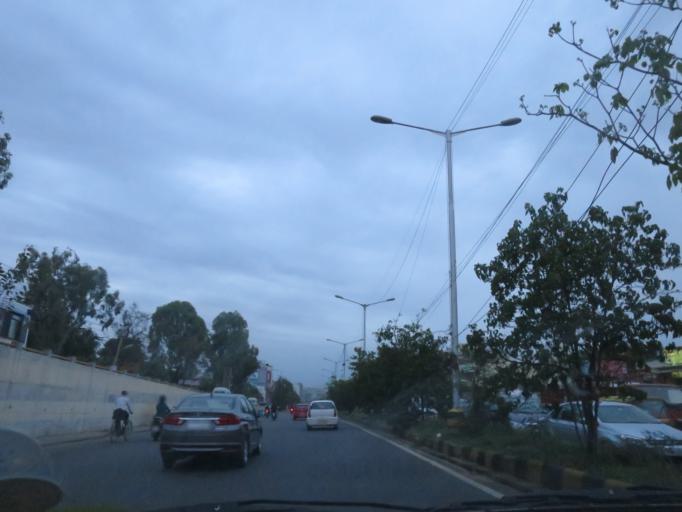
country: IN
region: Karnataka
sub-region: Bangalore Urban
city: Bangalore
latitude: 12.9554
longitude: 77.7007
